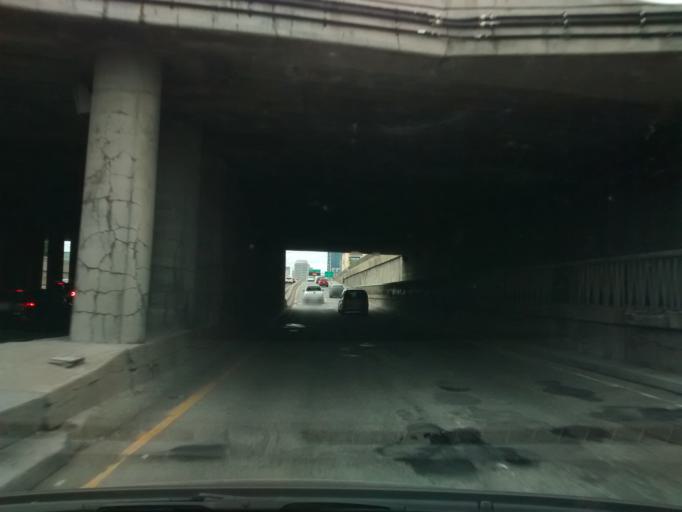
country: CA
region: Quebec
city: Mont-Royal
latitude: 45.5348
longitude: -73.6458
